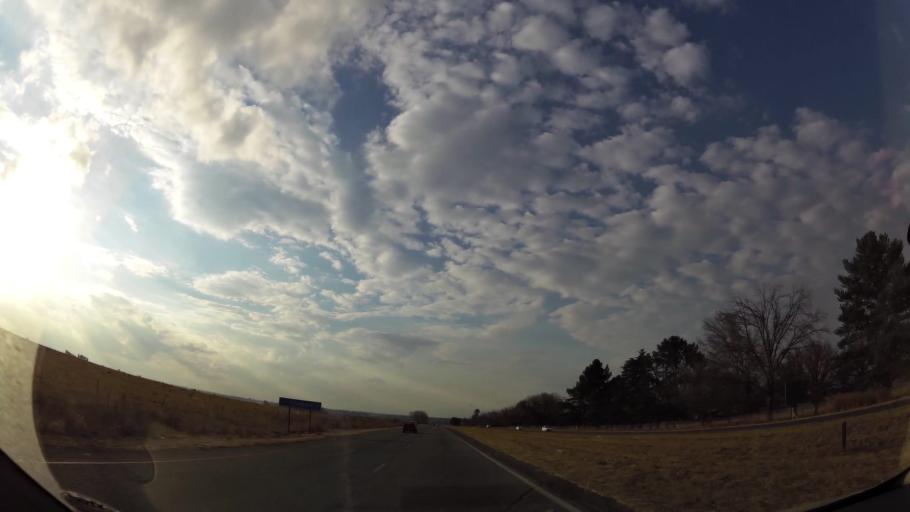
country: ZA
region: Orange Free State
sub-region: Fezile Dabi District Municipality
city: Sasolburg
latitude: -26.7739
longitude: 27.8247
